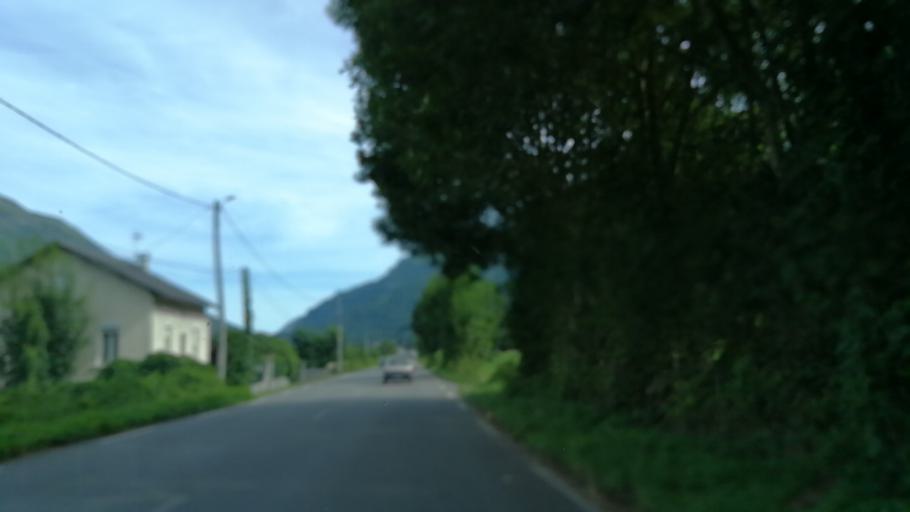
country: FR
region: Aquitaine
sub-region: Departement des Pyrenees-Atlantiques
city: Arette
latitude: 42.9865
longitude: -0.6043
